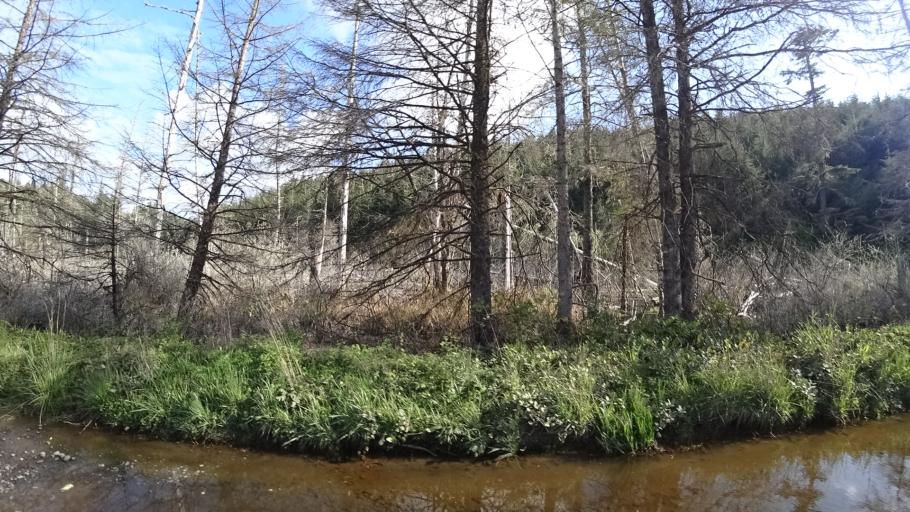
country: US
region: Oregon
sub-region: Douglas County
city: Reedsport
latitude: 43.7497
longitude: -124.1542
